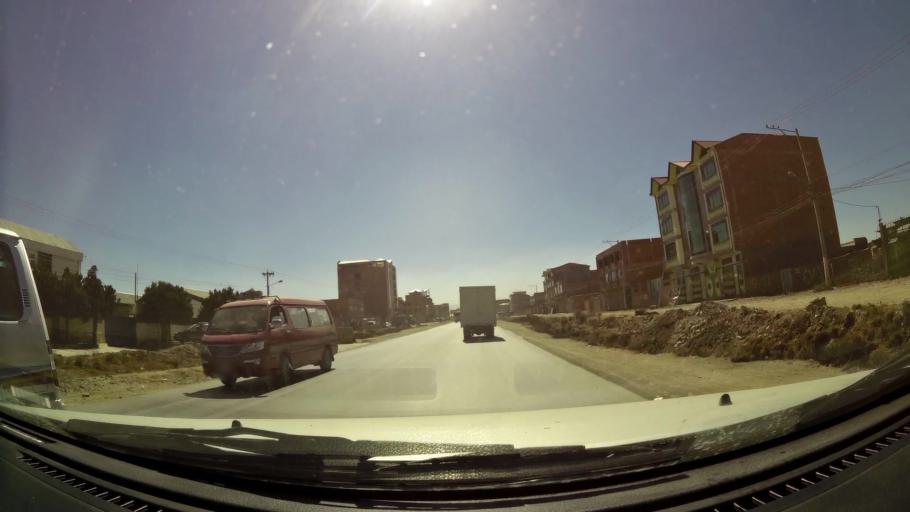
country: BO
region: La Paz
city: La Paz
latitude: -16.5541
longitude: -68.2087
